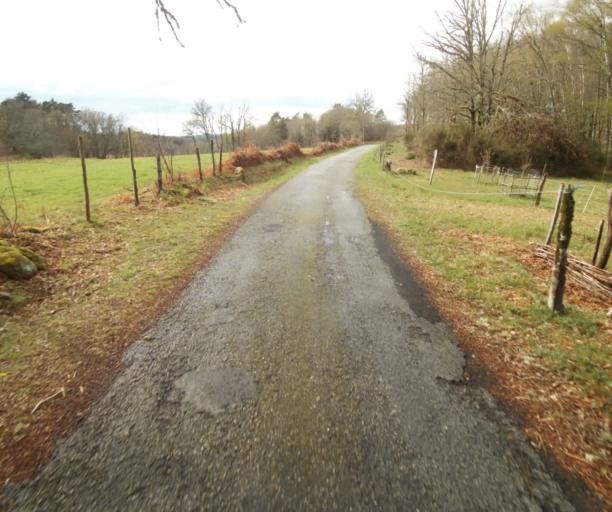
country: FR
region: Limousin
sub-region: Departement de la Correze
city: Saint-Privat
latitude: 45.2429
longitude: 2.0043
